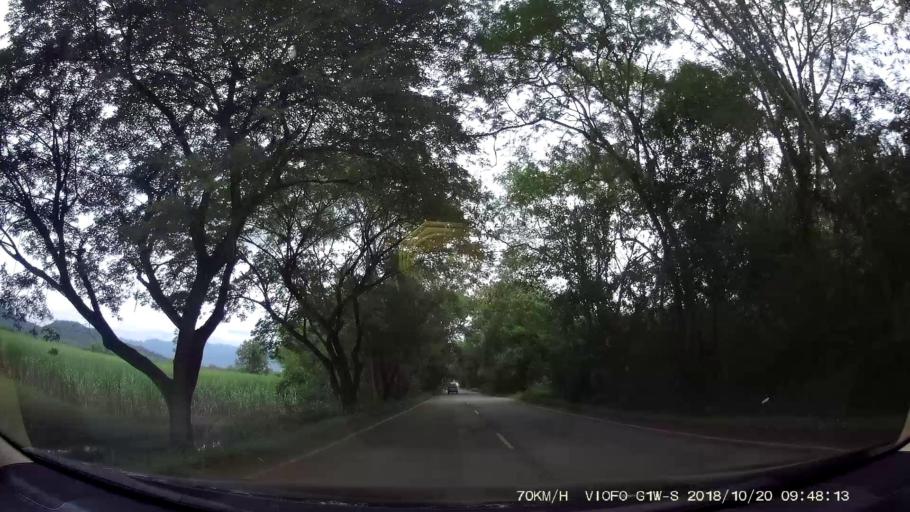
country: TH
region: Chaiyaphum
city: Khon San
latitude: 16.5096
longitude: 101.9137
